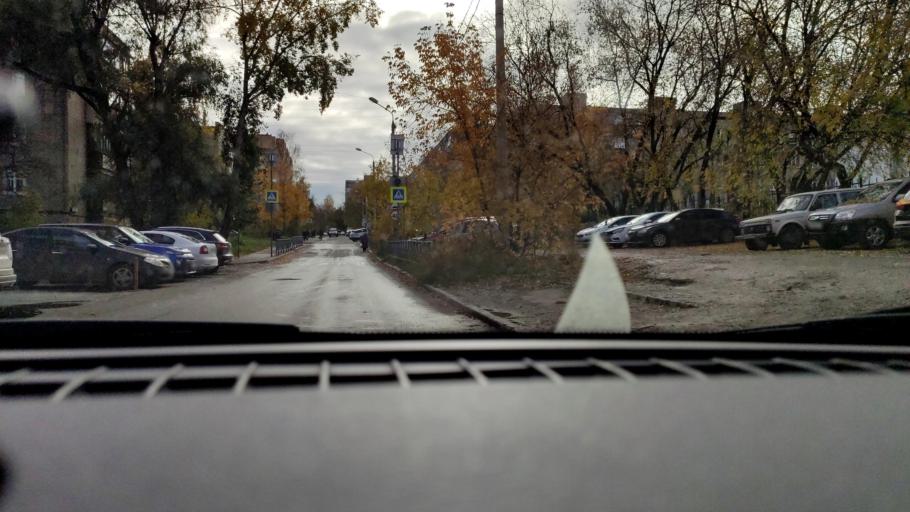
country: RU
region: Perm
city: Perm
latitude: 58.0044
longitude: 56.2710
